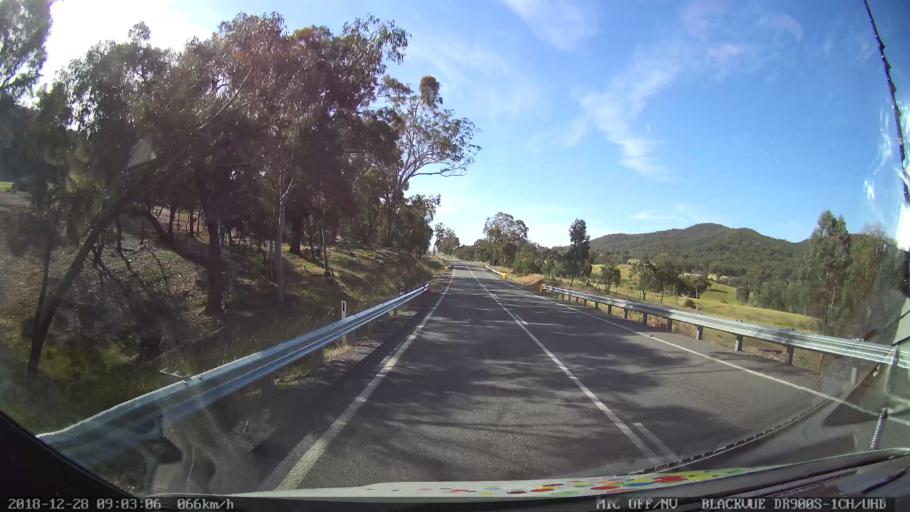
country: AU
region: New South Wales
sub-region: Upper Lachlan Shire
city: Crookwell
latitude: -34.1602
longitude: 149.3356
